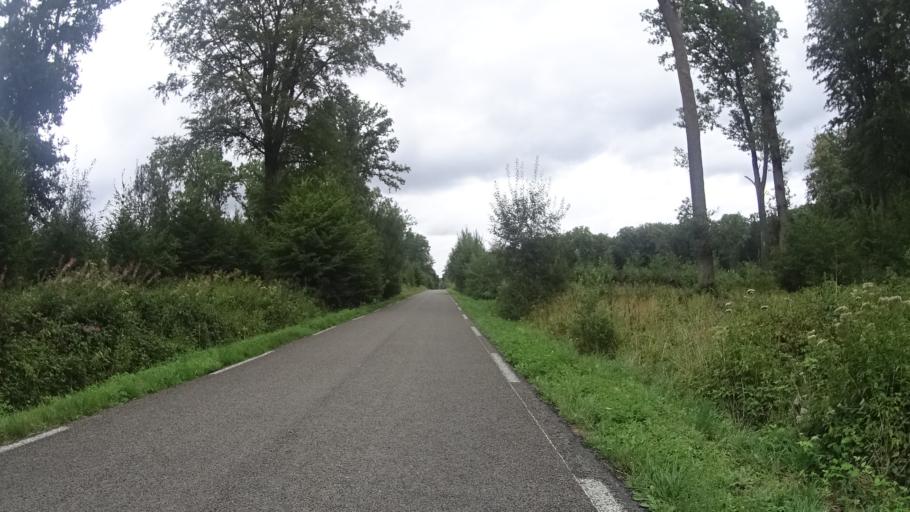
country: FR
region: Nord-Pas-de-Calais
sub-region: Departement du Nord
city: Maroilles
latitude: 50.1632
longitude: 3.7667
